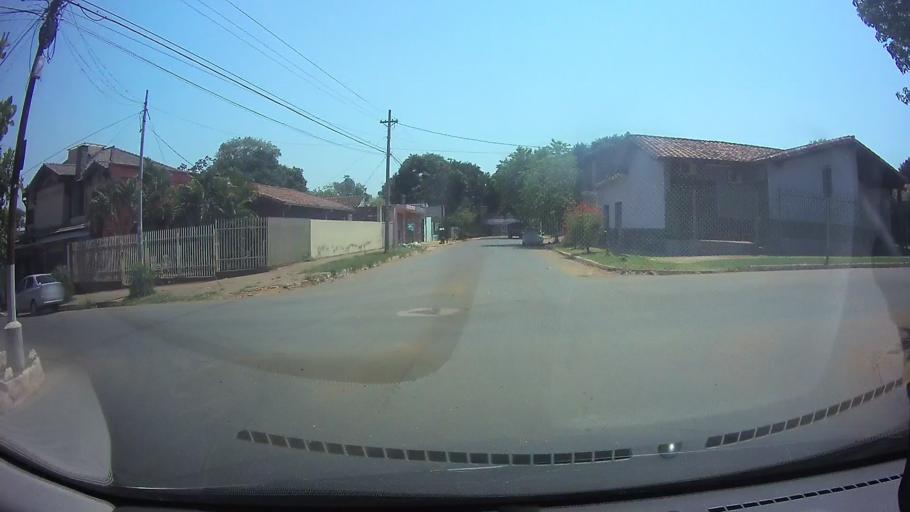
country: PY
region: Central
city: Fernando de la Mora
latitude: -25.3261
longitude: -57.5432
